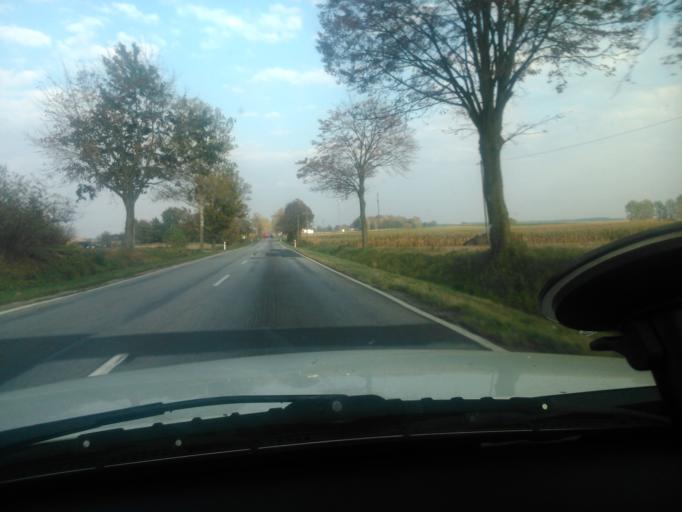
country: PL
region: Kujawsko-Pomorskie
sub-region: Powiat golubsko-dobrzynski
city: Golub-Dobrzyn
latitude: 53.1866
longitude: 19.0243
